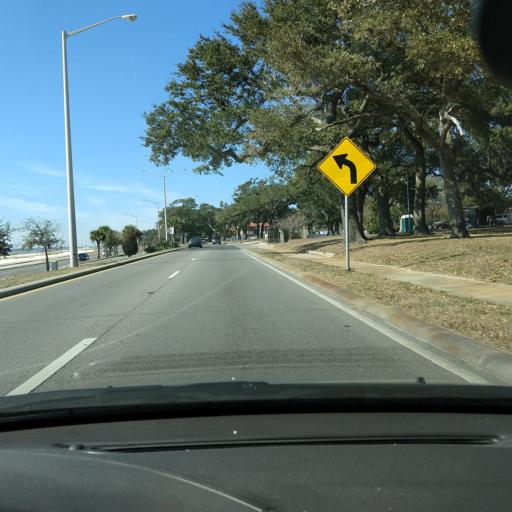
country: US
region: Mississippi
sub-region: Harrison County
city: Biloxi
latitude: 30.3946
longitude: -88.9219
